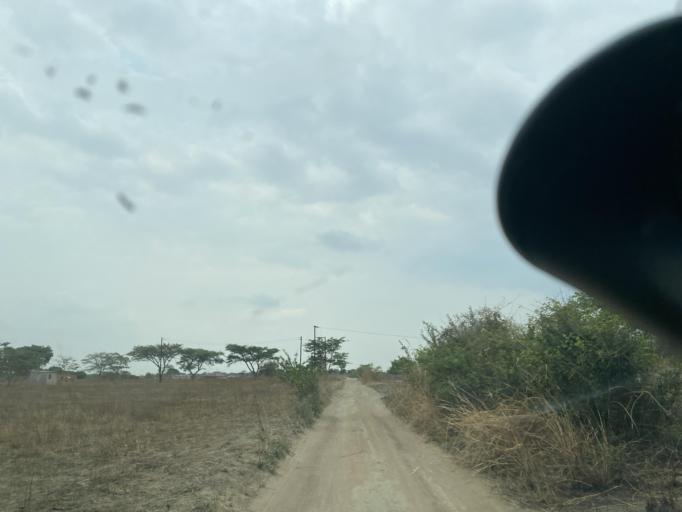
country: ZM
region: Lusaka
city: Lusaka
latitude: -15.2402
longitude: 28.3336
